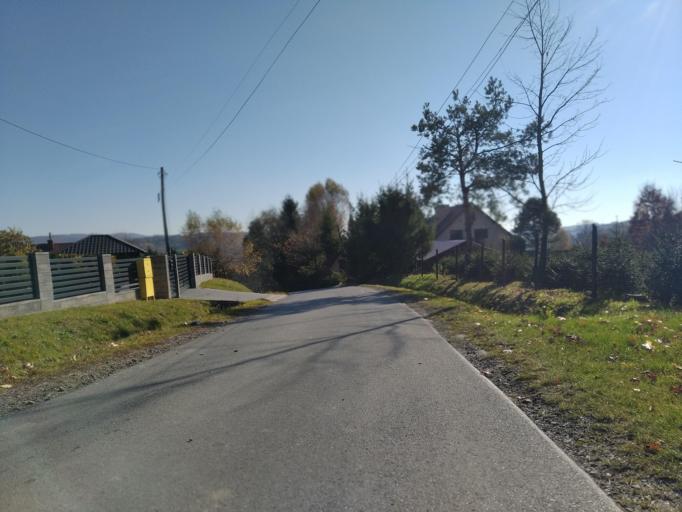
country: PL
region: Subcarpathian Voivodeship
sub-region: Powiat strzyzowski
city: Frysztak
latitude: 49.8436
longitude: 21.6063
